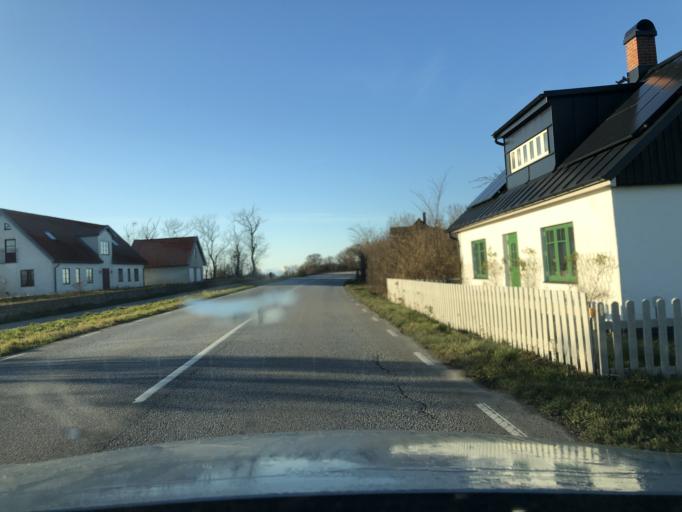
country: SE
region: Skane
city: Smygehamn
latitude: 55.3392
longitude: 13.3496
